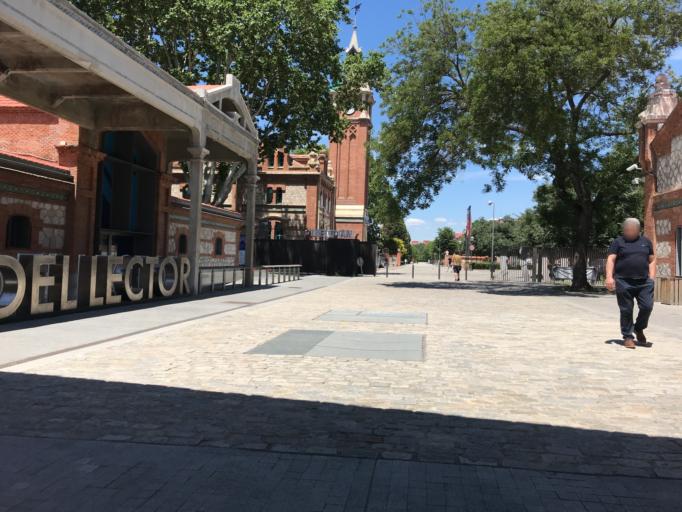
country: ES
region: Madrid
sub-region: Provincia de Madrid
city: Usera
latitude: 40.3927
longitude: -3.6983
